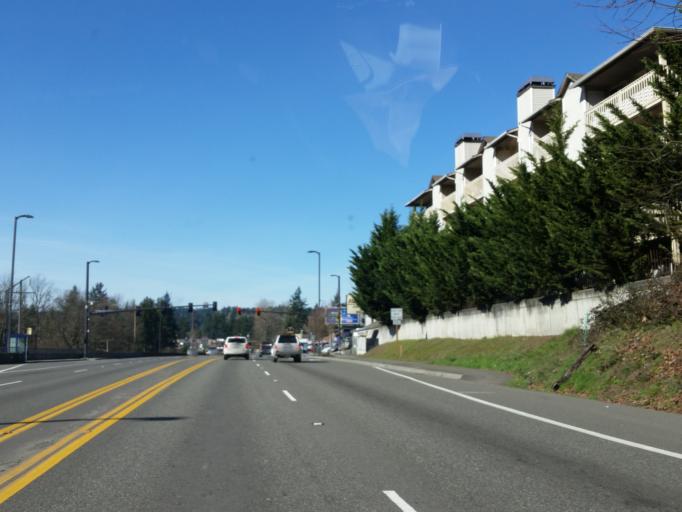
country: US
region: Washington
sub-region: King County
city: Kenmore
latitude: 47.7541
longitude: -122.2289
